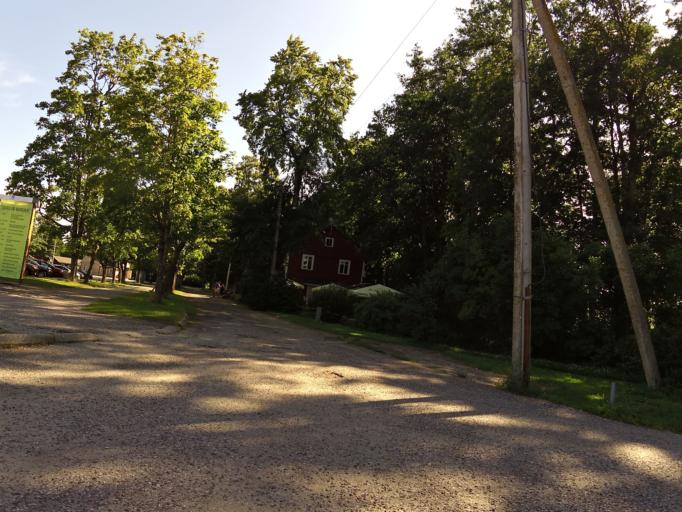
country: EE
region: Hiiumaa
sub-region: Kaerdla linn
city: Kardla
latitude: 58.9981
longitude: 22.7464
